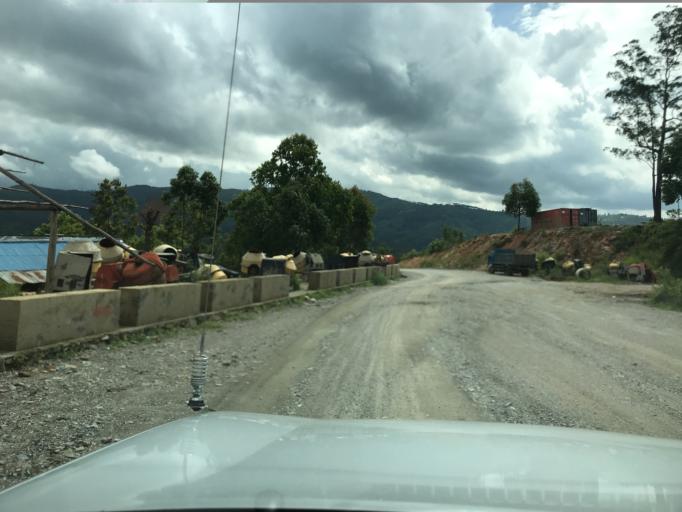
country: TL
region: Aileu
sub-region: Aileu Villa
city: Aileu
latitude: -8.6634
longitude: 125.5435
